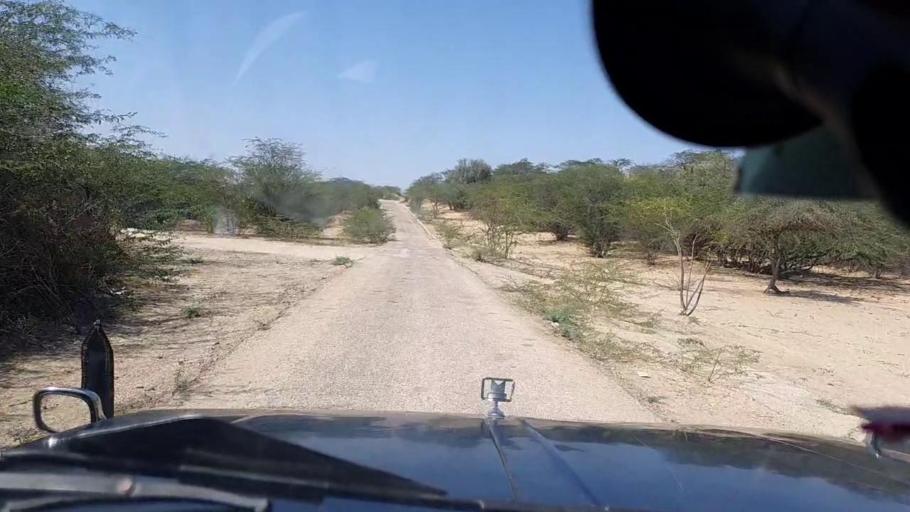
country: PK
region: Sindh
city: Mithi
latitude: 24.6132
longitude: 69.6851
